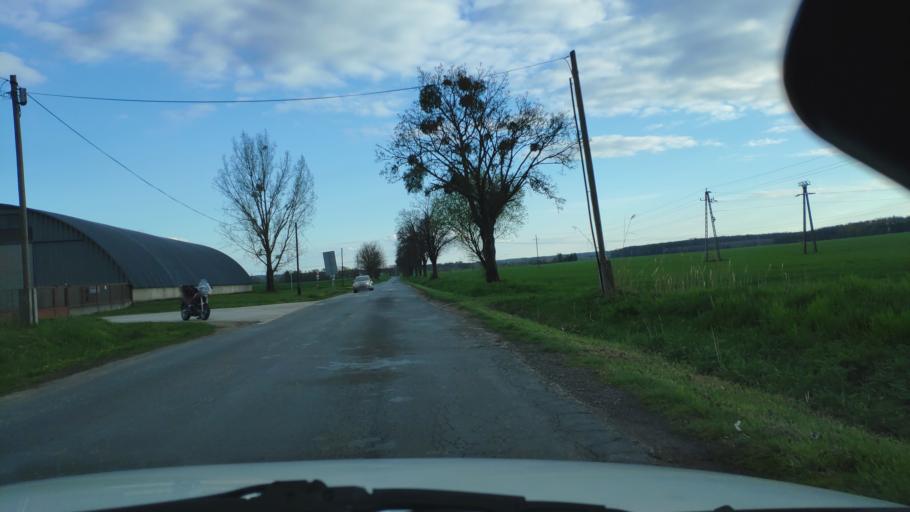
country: HU
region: Zala
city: Zalakomar
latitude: 46.5103
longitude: 17.1231
